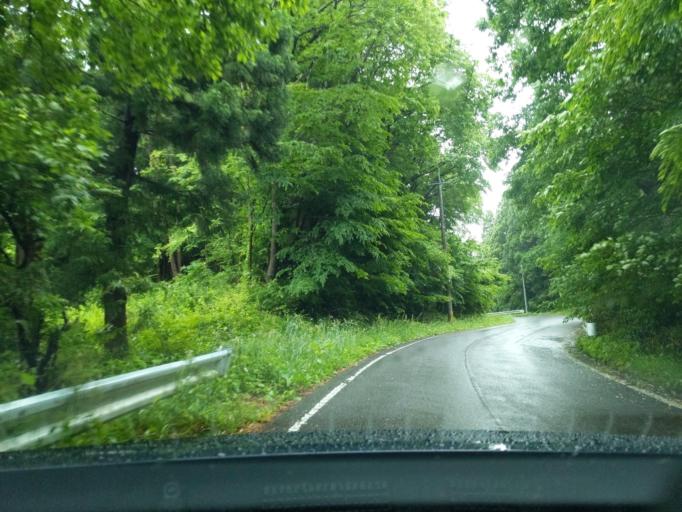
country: JP
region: Fukushima
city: Nihommatsu
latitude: 37.5970
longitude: 140.5719
